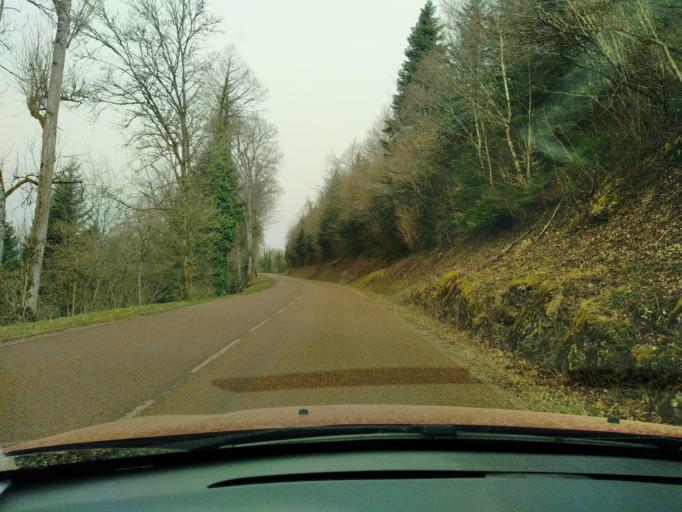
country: FR
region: Franche-Comte
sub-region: Departement du Jura
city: Clairvaux-les-Lacs
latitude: 46.6410
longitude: 5.7533
